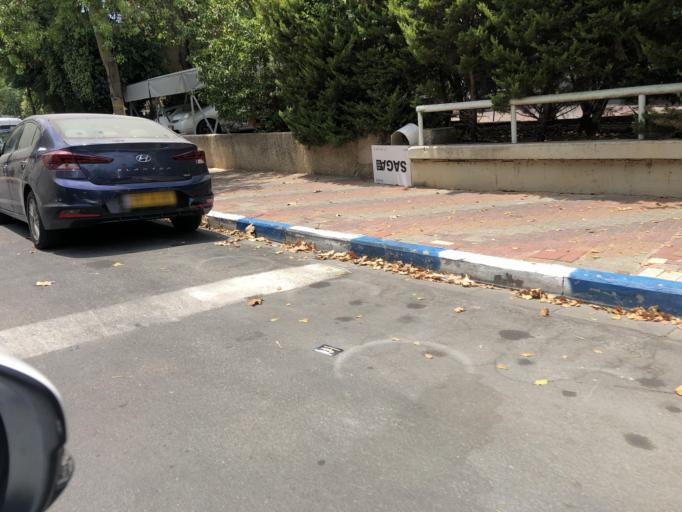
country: IL
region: Tel Aviv
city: Bene Beraq
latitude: 32.0624
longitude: 34.8325
